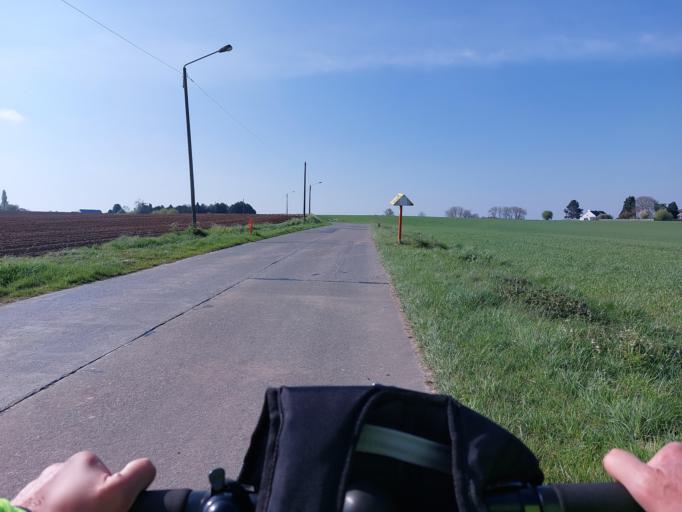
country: BE
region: Wallonia
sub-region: Province du Hainaut
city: Ecaussinnes-d'Enghien
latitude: 50.5344
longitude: 4.1470
